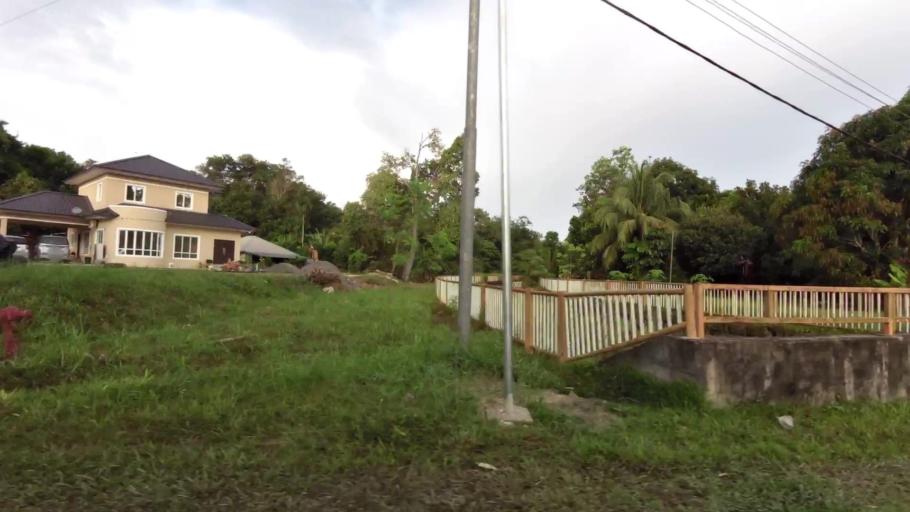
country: BN
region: Brunei and Muara
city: Bandar Seri Begawan
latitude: 4.9779
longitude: 114.9894
